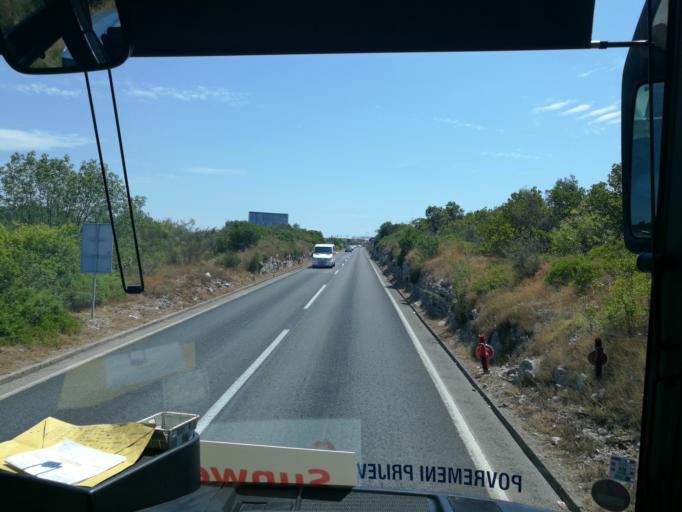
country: HR
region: Dubrovacko-Neretvanska
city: Cavtat
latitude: 42.5727
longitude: 18.2419
